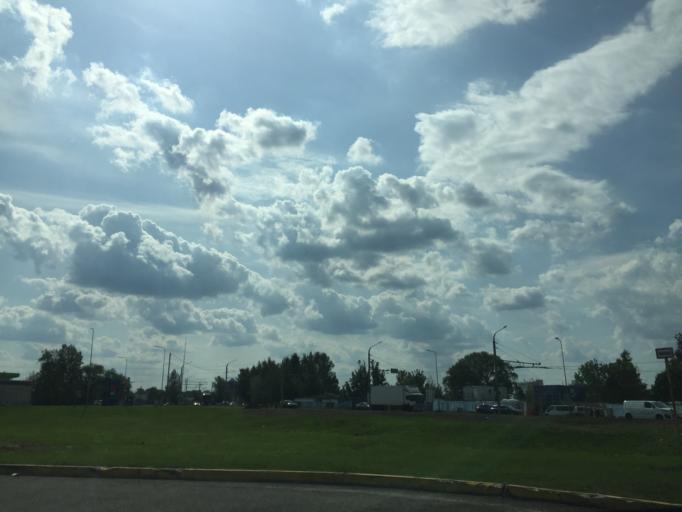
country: LV
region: Riga
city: Riga
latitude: 56.9260
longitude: 24.1108
